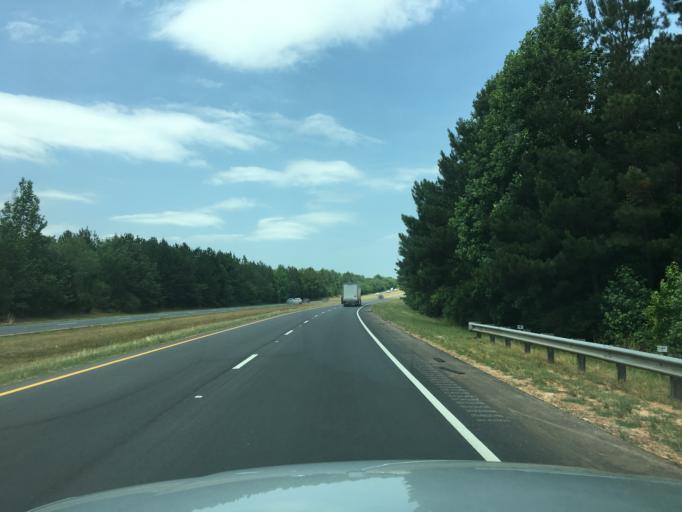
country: US
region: Georgia
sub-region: Jackson County
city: Commerce
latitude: 34.2238
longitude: -83.4492
